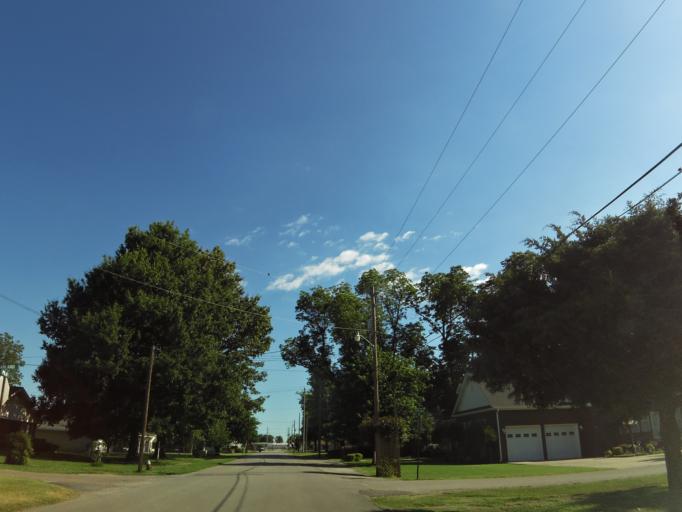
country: US
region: Arkansas
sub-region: Clay County
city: Corning
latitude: 36.4094
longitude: -90.5876
